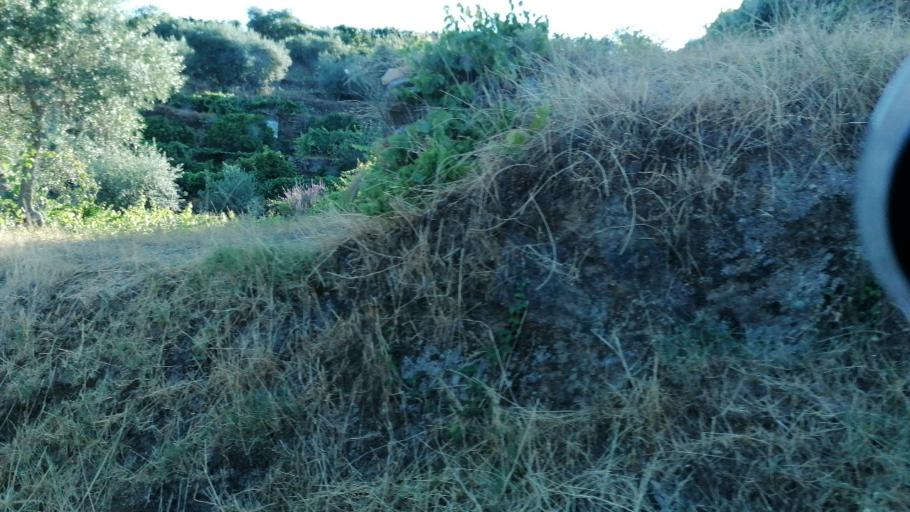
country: PT
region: Viseu
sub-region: Sao Joao da Pesqueira
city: Sao Joao da Pesqueira
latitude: 41.2397
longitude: -7.4312
